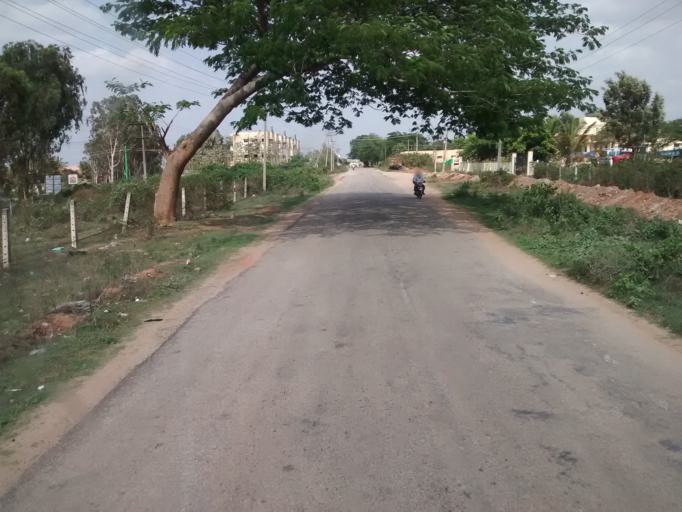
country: IN
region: Karnataka
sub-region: Mysore
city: Hunsur
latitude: 12.3366
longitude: 76.4472
